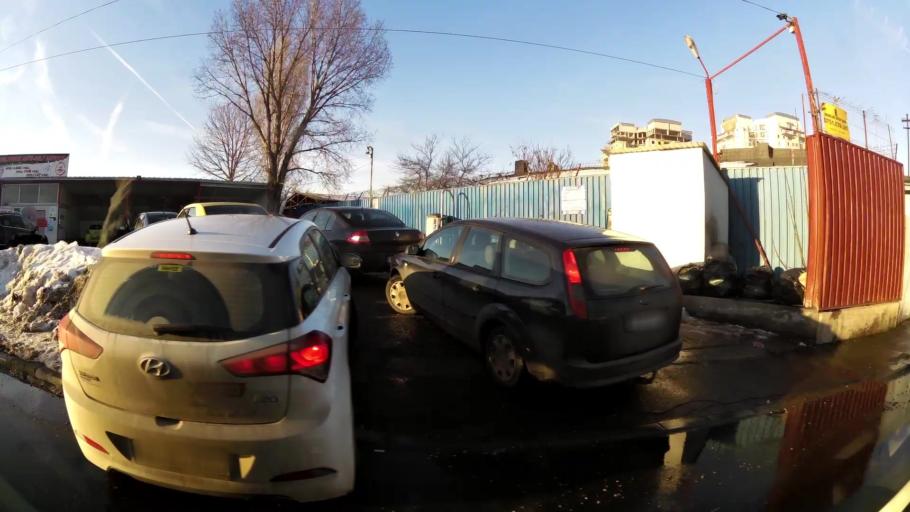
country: RO
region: Ilfov
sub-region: Comuna Fundeni-Dobroesti
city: Fundeni
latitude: 44.4531
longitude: 26.1413
